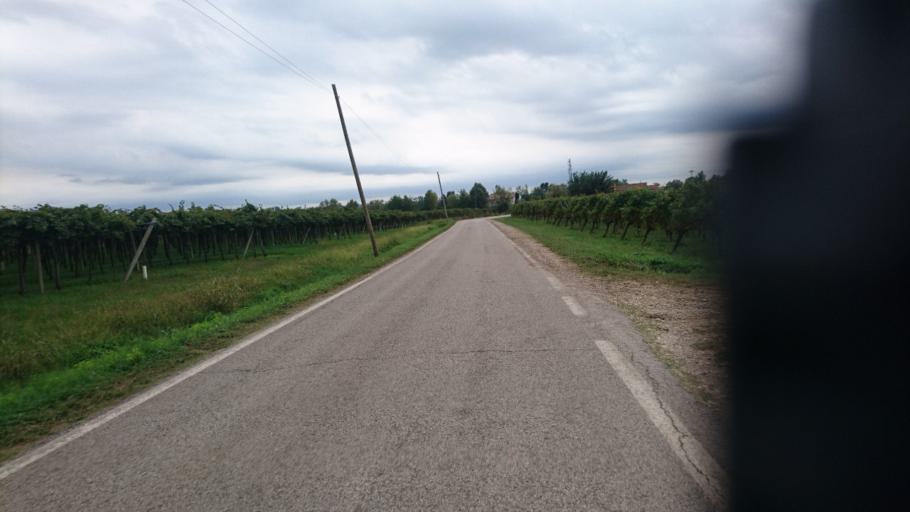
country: IT
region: Veneto
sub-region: Provincia di Vicenza
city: Gambellara
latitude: 45.4366
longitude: 11.3417
